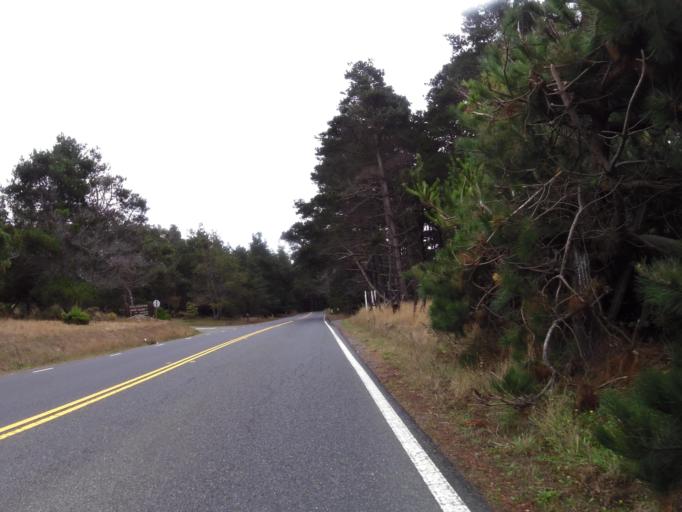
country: US
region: California
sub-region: Sonoma County
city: Sea Ranch
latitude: 38.5461
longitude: -123.2966
